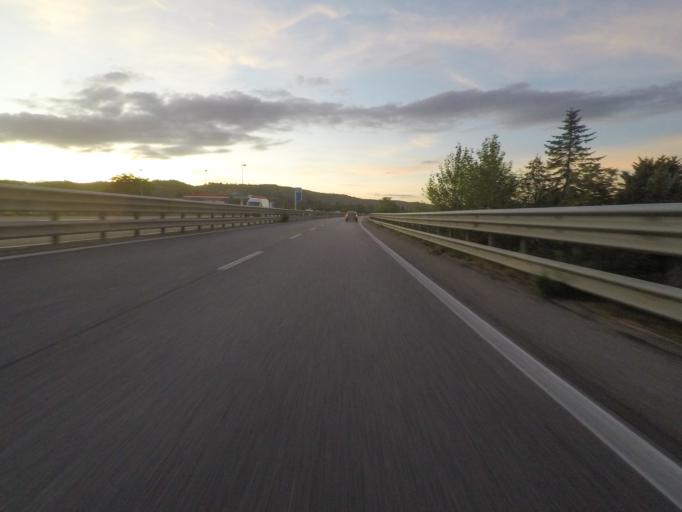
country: IT
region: Tuscany
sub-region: Provincia di Siena
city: Sinalunga
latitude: 43.2270
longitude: 11.7376
